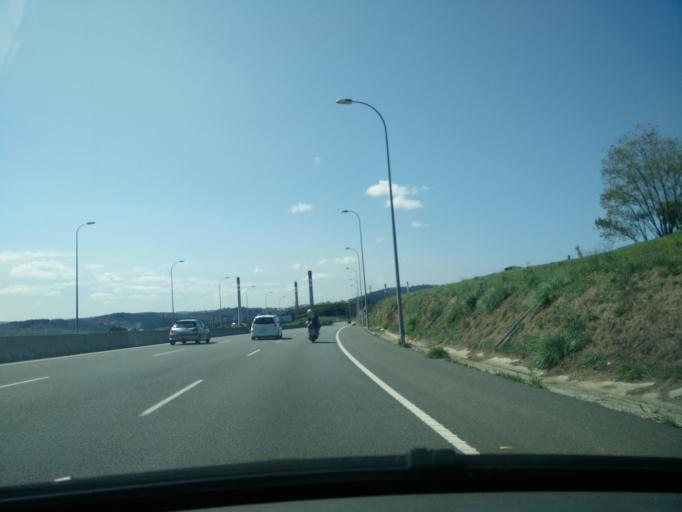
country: ES
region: Galicia
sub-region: Provincia da Coruna
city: A Coruna
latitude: 43.3588
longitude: -8.4332
